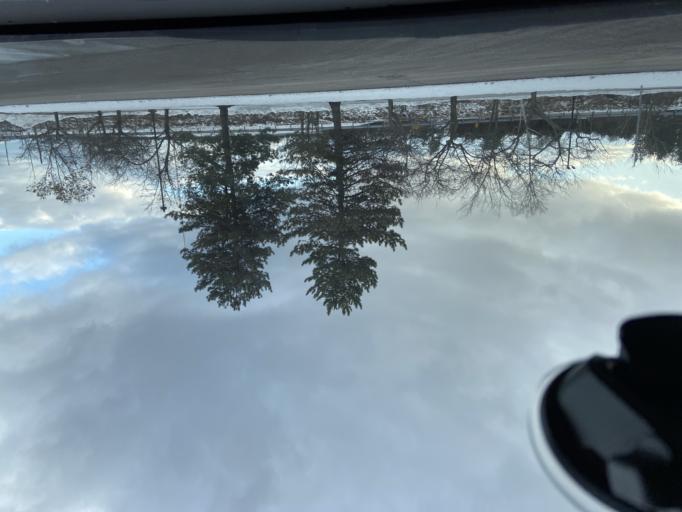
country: US
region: Massachusetts
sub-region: Norfolk County
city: Needham
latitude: 42.3013
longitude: -71.2217
